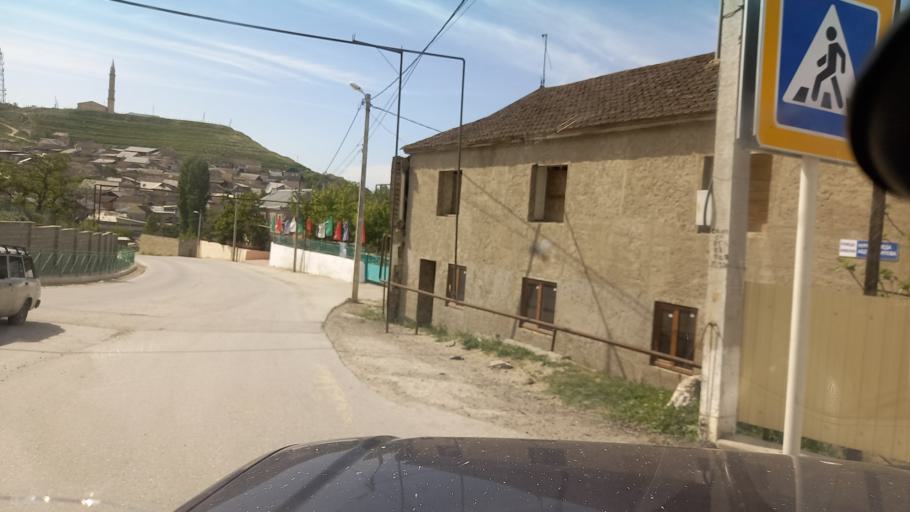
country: RU
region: Dagestan
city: Karabudakhkent
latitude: 42.7085
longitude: 47.5708
